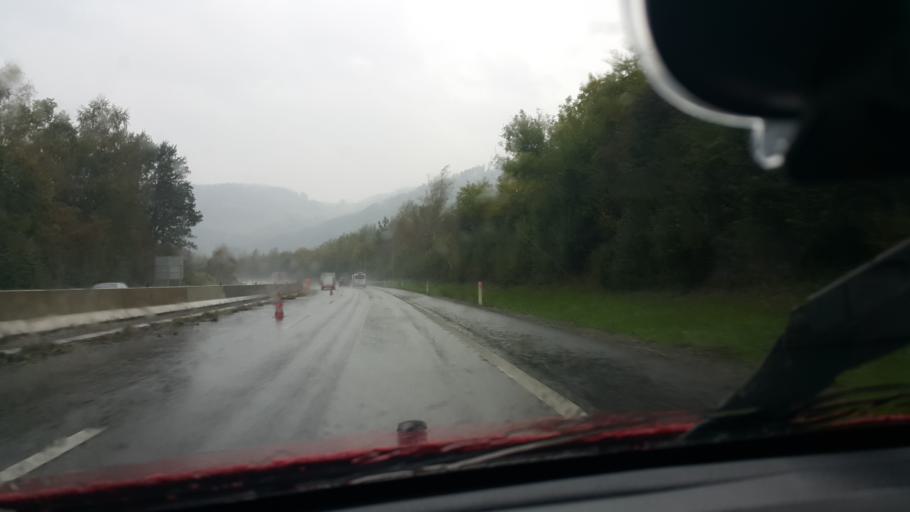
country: AT
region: Carinthia
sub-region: Politischer Bezirk Volkermarkt
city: Griffen
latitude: 46.6970
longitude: 14.7293
